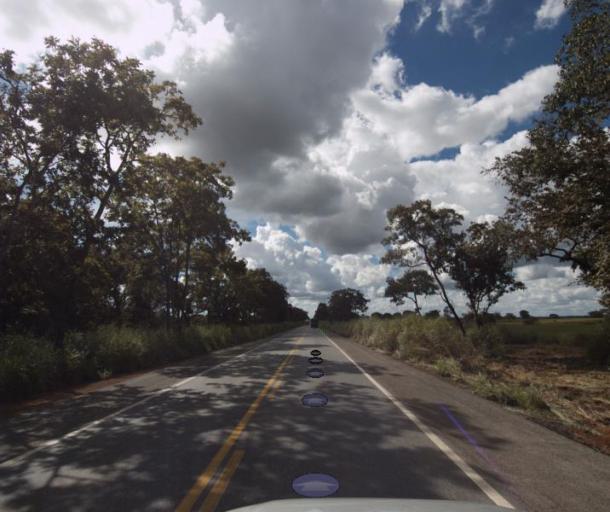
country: BR
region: Goias
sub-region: Porangatu
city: Porangatu
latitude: -13.2969
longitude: -49.1226
